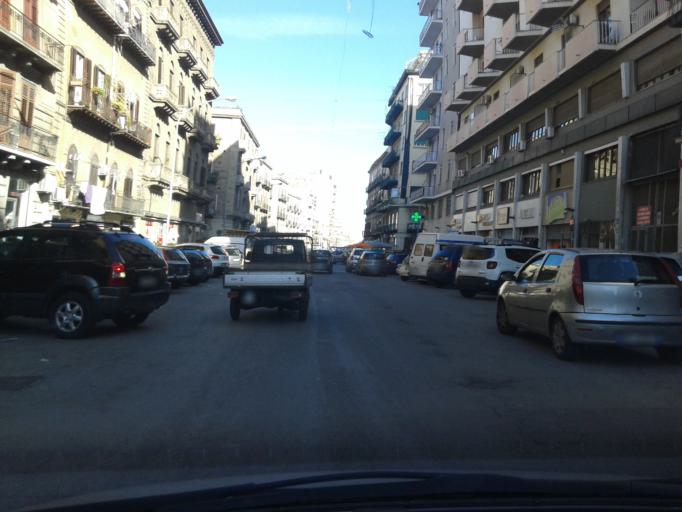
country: IT
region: Sicily
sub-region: Palermo
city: Palermo
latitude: 38.1186
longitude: 13.3474
